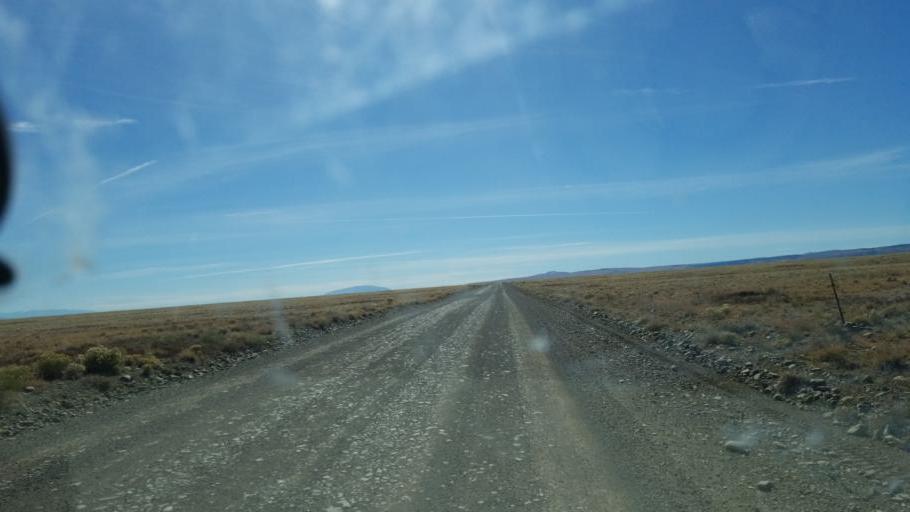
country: US
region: Colorado
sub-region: Rio Grande County
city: Monte Vista
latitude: 37.3525
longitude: -106.1491
